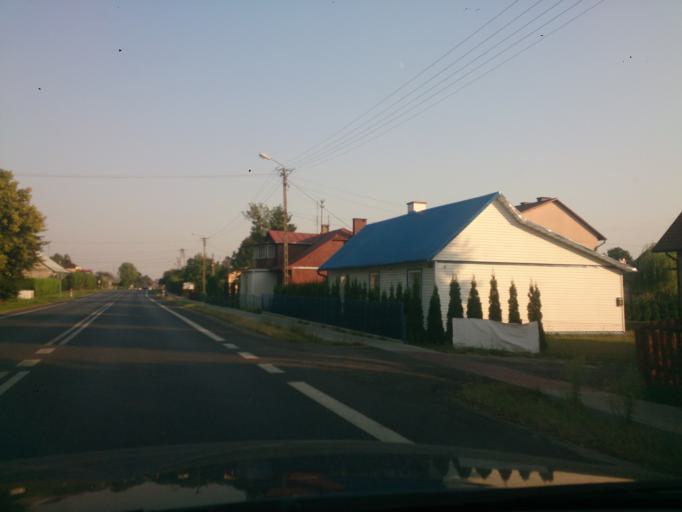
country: PL
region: Subcarpathian Voivodeship
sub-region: Powiat kolbuszowski
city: Kolbuszowa
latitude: 50.2558
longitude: 21.7689
